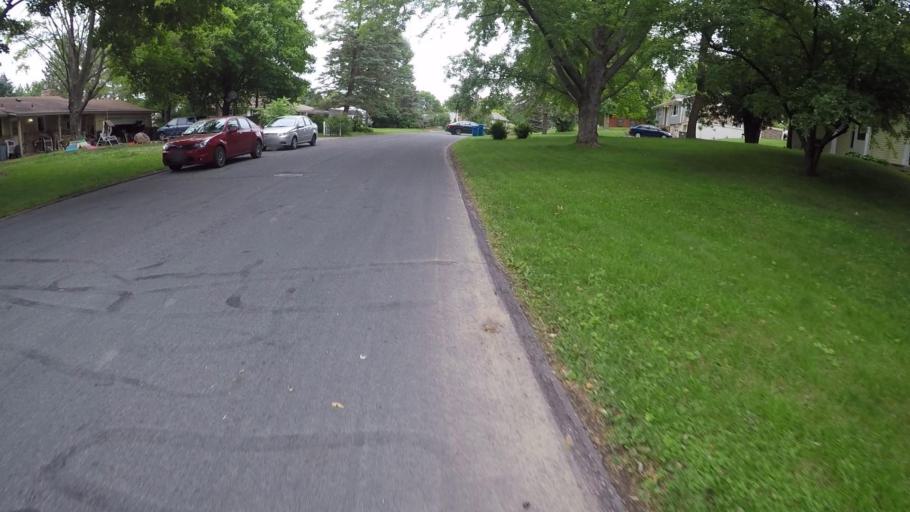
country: US
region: Minnesota
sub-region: Carver County
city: Chanhassen
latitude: 44.8784
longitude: -93.5086
